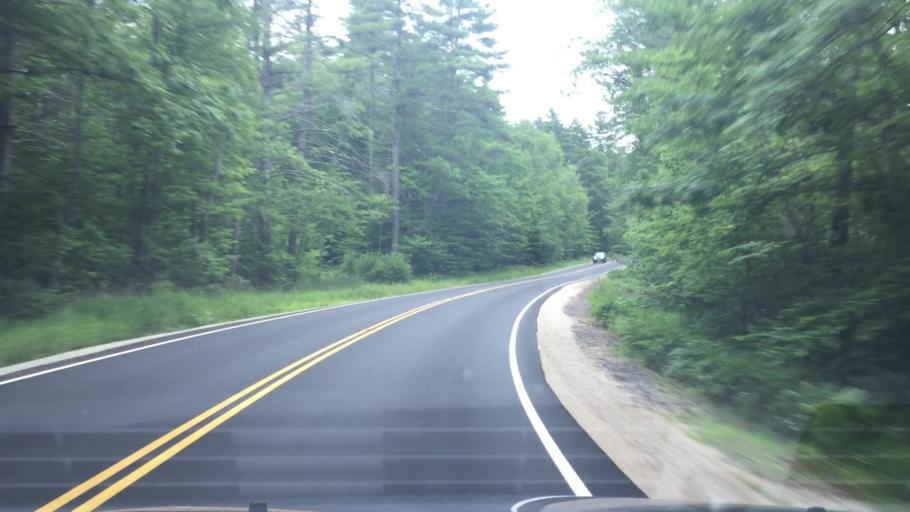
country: US
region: New Hampshire
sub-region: Carroll County
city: Freedom
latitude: 43.8427
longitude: -71.0831
